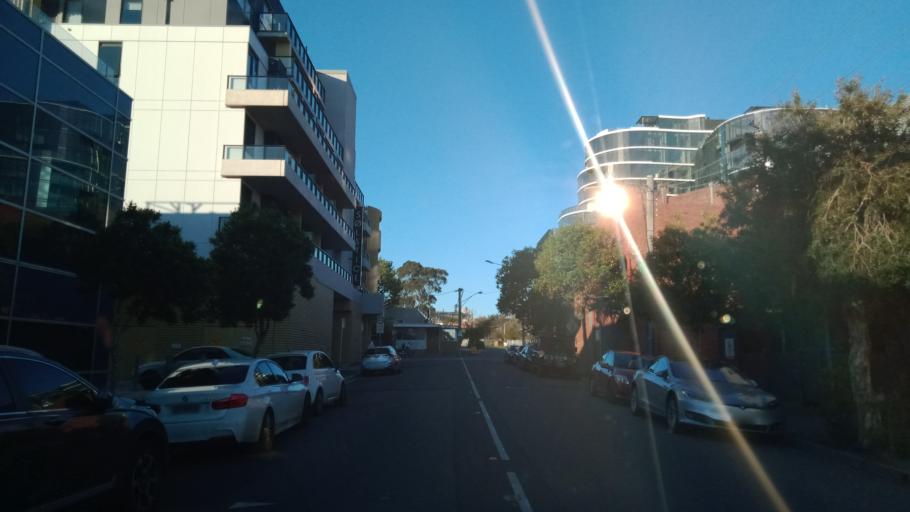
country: AU
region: Victoria
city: Glenferrie
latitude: -37.8294
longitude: 145.0533
